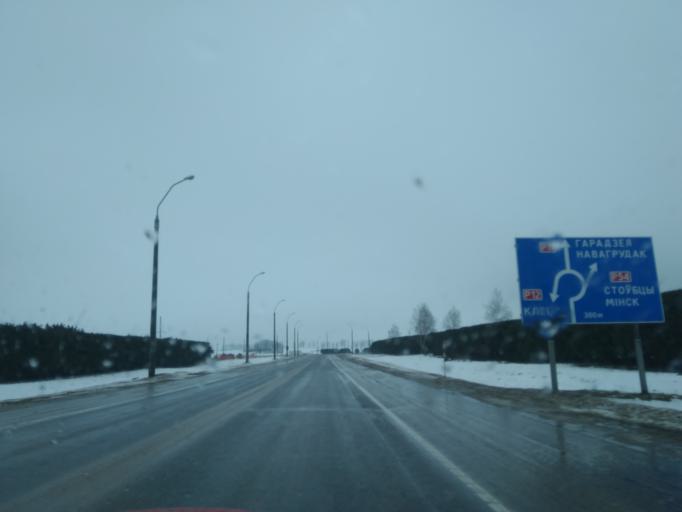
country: BY
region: Minsk
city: Nyasvizh
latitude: 53.2372
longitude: 26.6380
